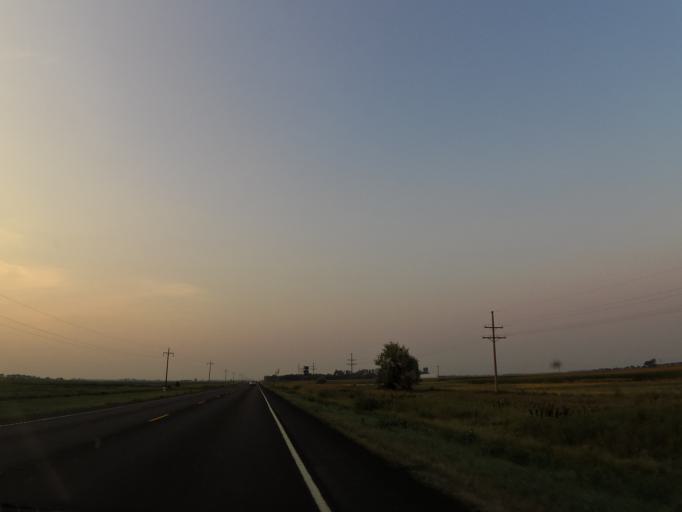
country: US
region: North Dakota
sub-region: Walsh County
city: Park River
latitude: 48.2211
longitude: -97.6225
